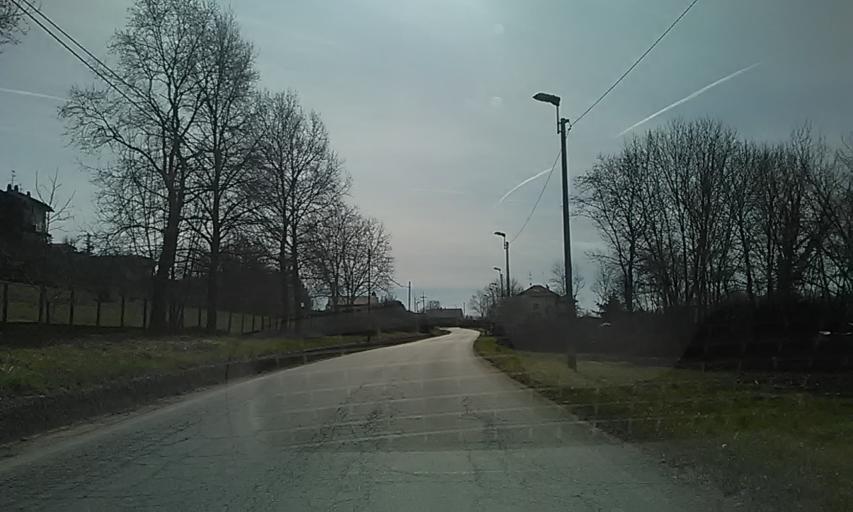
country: IT
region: Piedmont
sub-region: Provincia di Biella
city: Brusnengo
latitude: 45.6009
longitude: 8.2447
